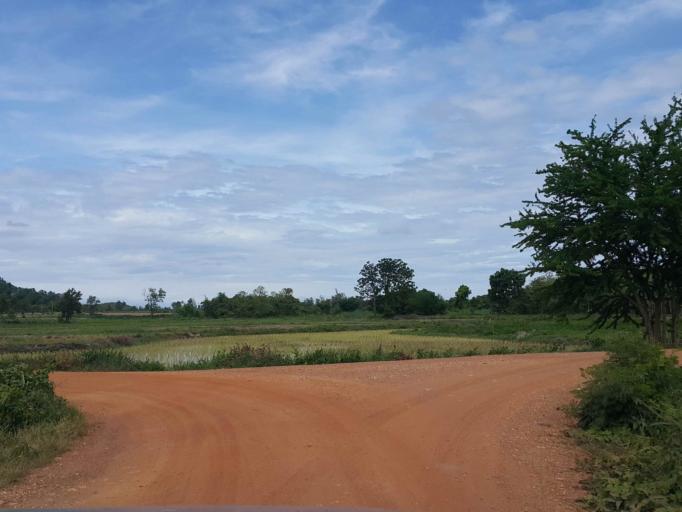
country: TH
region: Sukhothai
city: Ban Dan Lan Hoi
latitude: 17.1034
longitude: 99.4689
